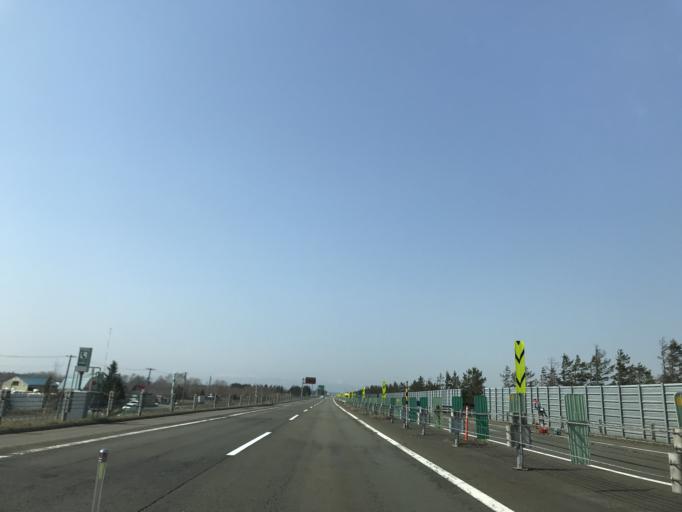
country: JP
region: Hokkaido
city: Ebetsu
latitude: 43.1094
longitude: 141.6088
